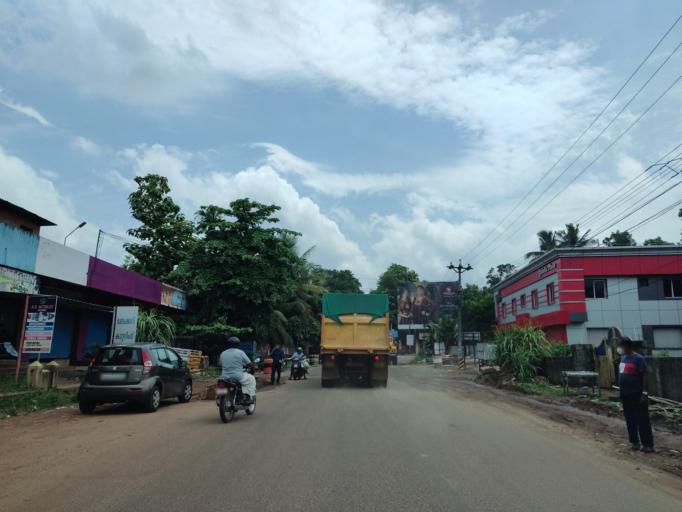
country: IN
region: Kerala
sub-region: Alappuzha
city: Mavelikara
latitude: 9.2272
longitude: 76.6121
